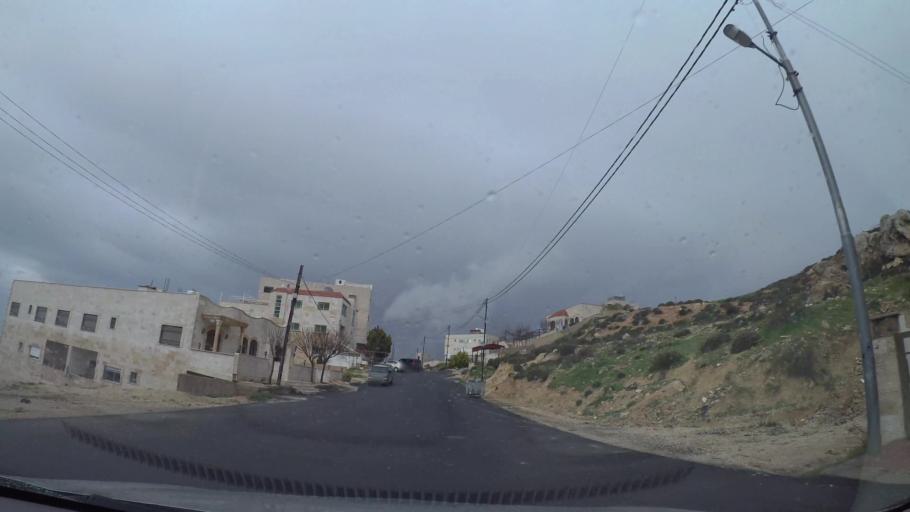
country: JO
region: Amman
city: Al Jubayhah
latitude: 32.0347
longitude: 35.8427
